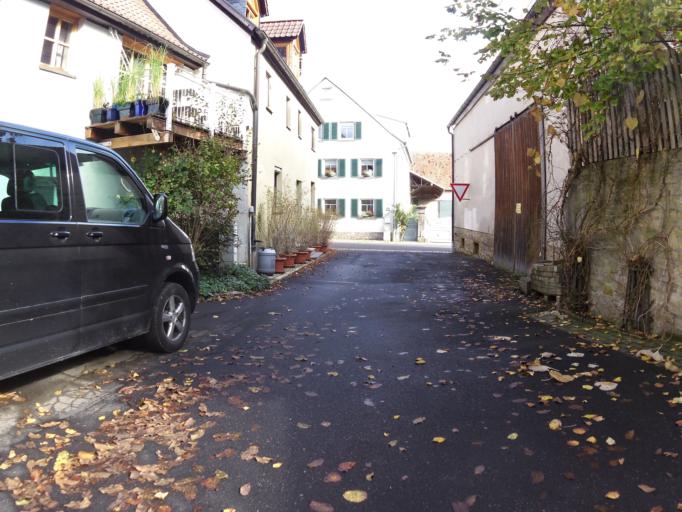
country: DE
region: Bavaria
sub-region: Regierungsbezirk Unterfranken
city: Frickenhausen
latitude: 49.7061
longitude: 10.0801
